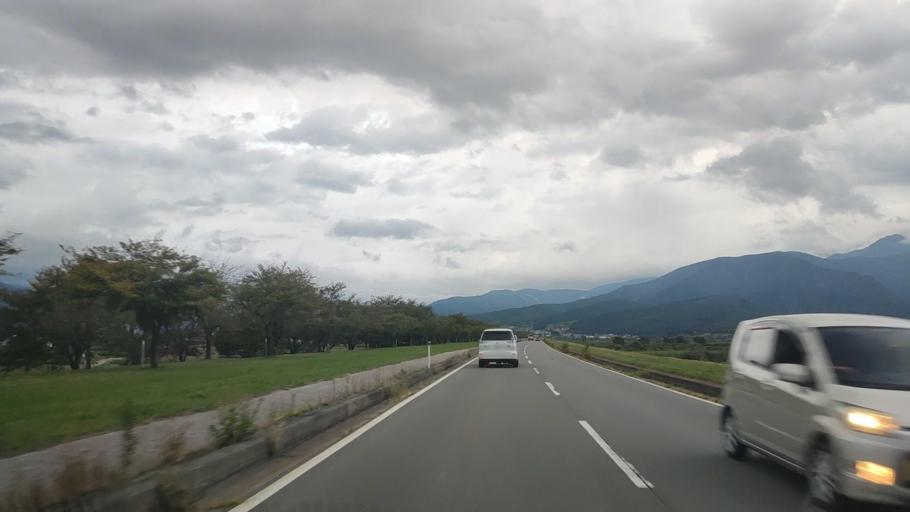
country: JP
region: Nagano
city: Iiyama
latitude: 36.8728
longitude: 138.3770
